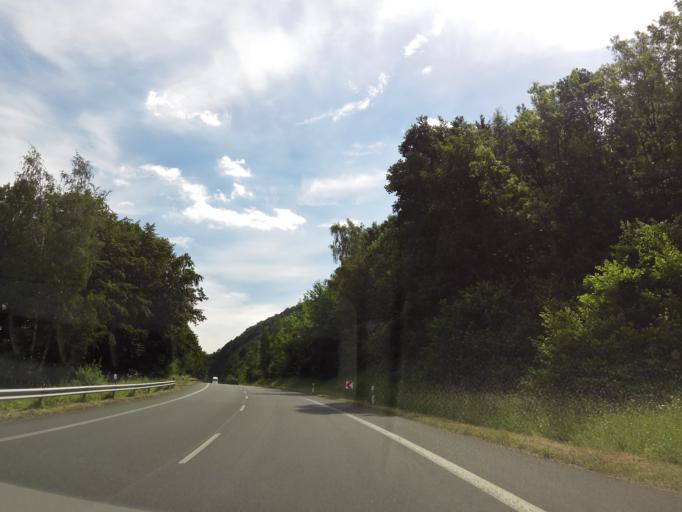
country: DE
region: North Rhine-Westphalia
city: Beverungen
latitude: 51.6352
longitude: 9.3835
